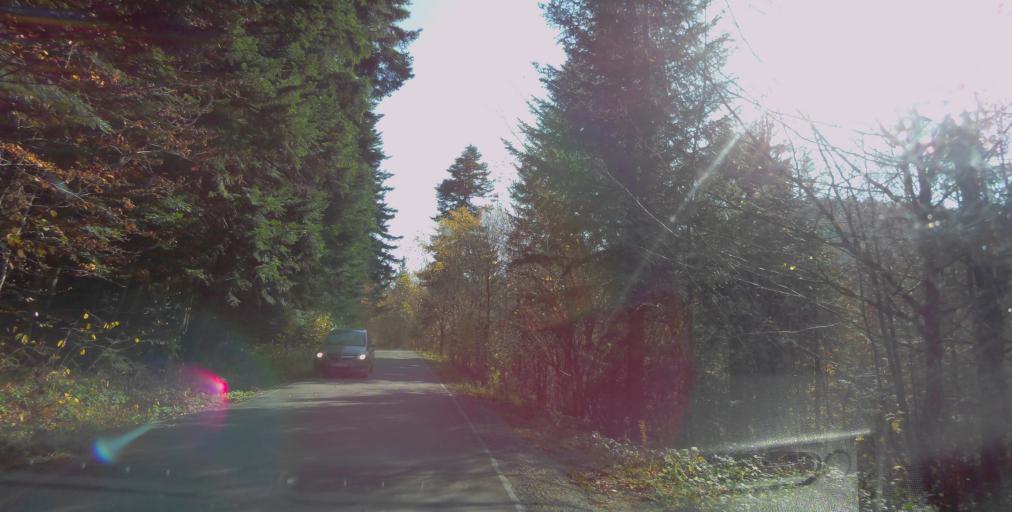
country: PL
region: Subcarpathian Voivodeship
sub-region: Powiat leski
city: Polanczyk
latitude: 49.3139
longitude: 22.4454
